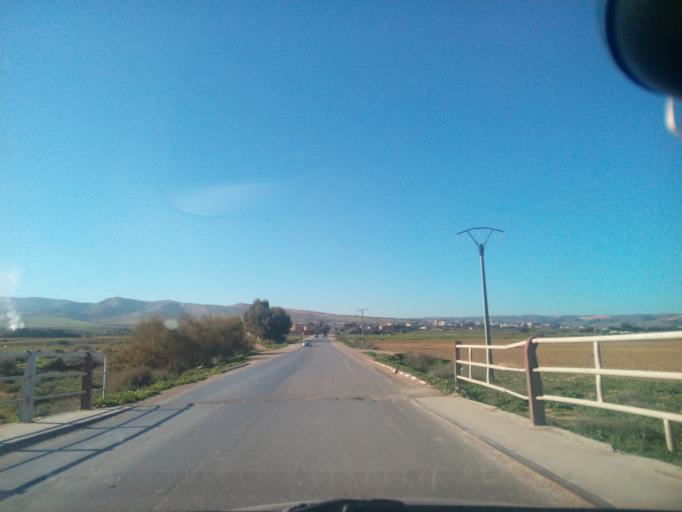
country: DZ
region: Relizane
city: Relizane
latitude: 35.8990
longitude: 0.5368
